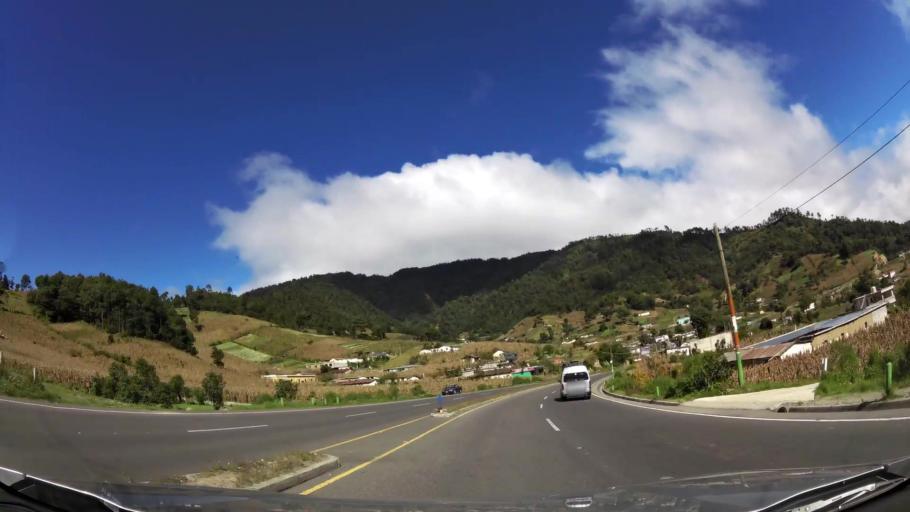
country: GT
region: Solola
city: Solola
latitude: 14.8307
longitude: -91.1846
